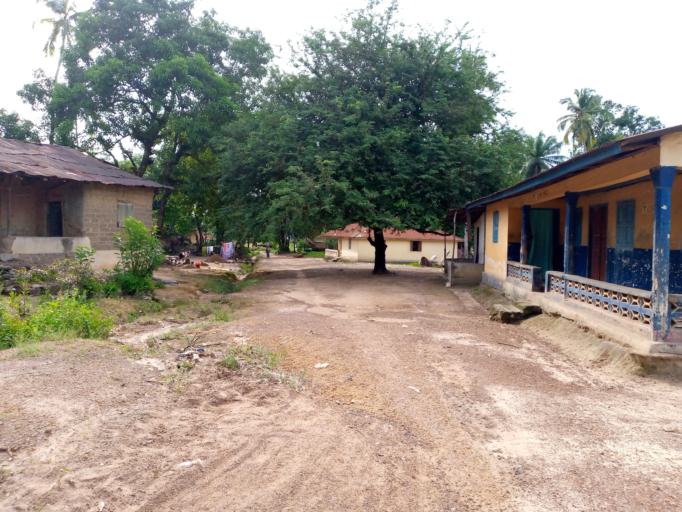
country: SL
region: Northern Province
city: Magburaka
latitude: 8.7183
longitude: -11.9502
